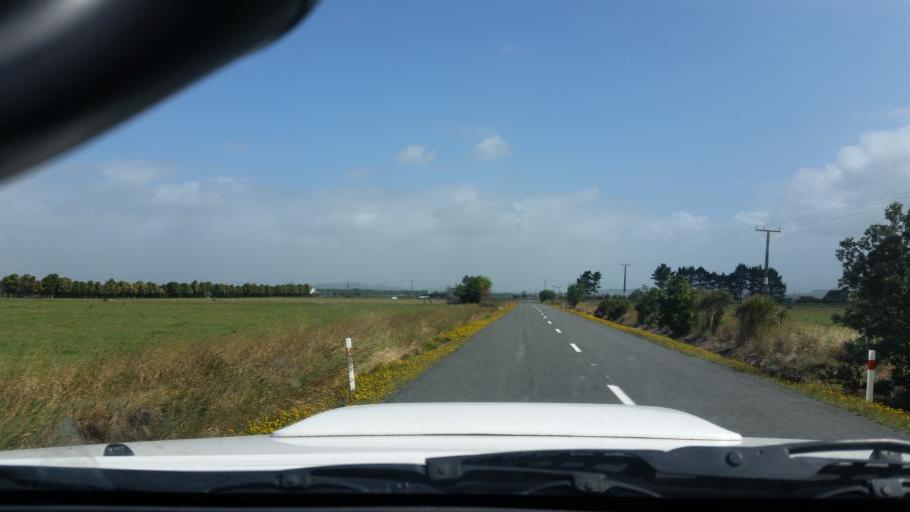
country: NZ
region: Northland
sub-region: Kaipara District
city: Dargaville
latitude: -36.1244
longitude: 174.0511
